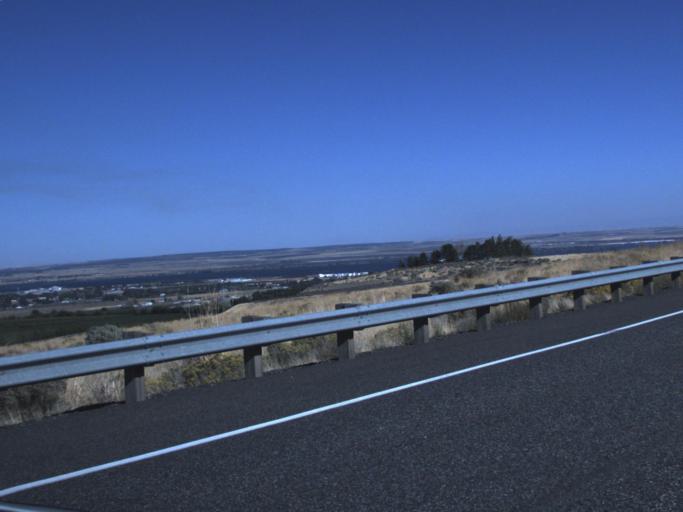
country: US
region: Washington
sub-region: Benton County
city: Highland
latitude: 46.1282
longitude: -119.0726
